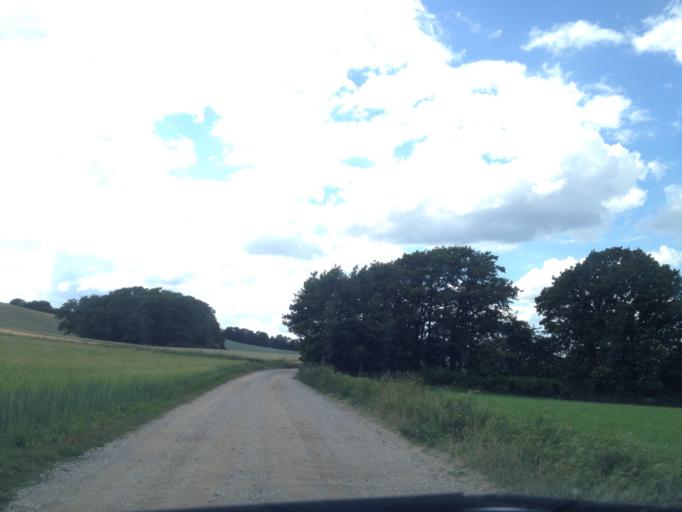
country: DK
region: Central Jutland
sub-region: Syddjurs Kommune
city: Ronde
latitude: 56.1983
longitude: 10.4898
